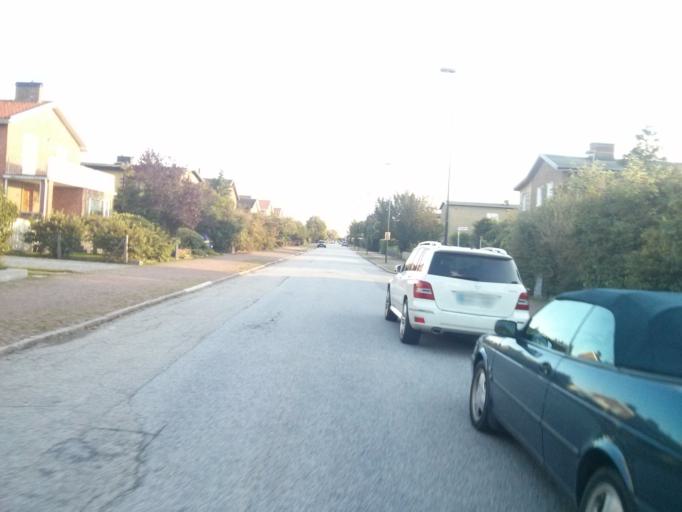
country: SE
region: Skane
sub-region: Malmo
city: Malmoe
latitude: 55.5823
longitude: 12.9589
